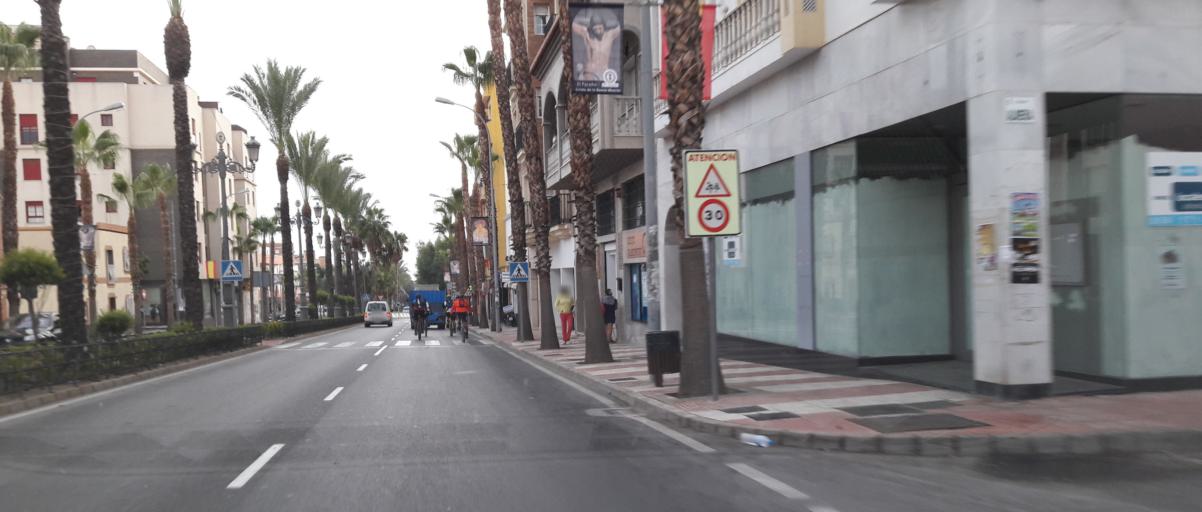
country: ES
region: Andalusia
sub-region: Provincia de Almeria
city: Aguadulce
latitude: 36.8077
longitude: -2.5982
